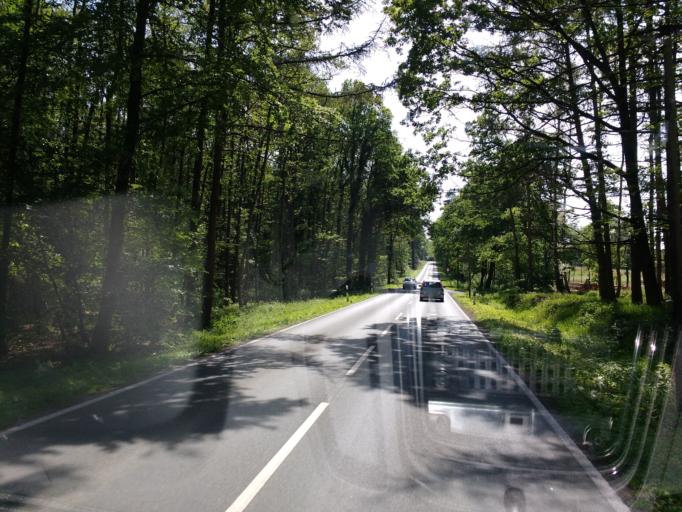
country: DE
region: Lower Saxony
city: Belm
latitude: 52.3269
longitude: 8.1177
